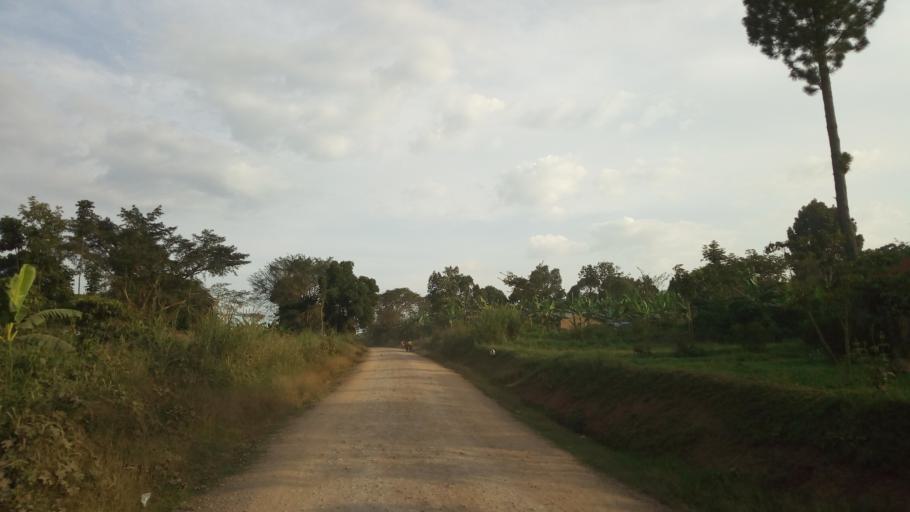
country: UG
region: Central Region
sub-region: Kiboga District
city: Kiboga
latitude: 0.7036
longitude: 31.7792
